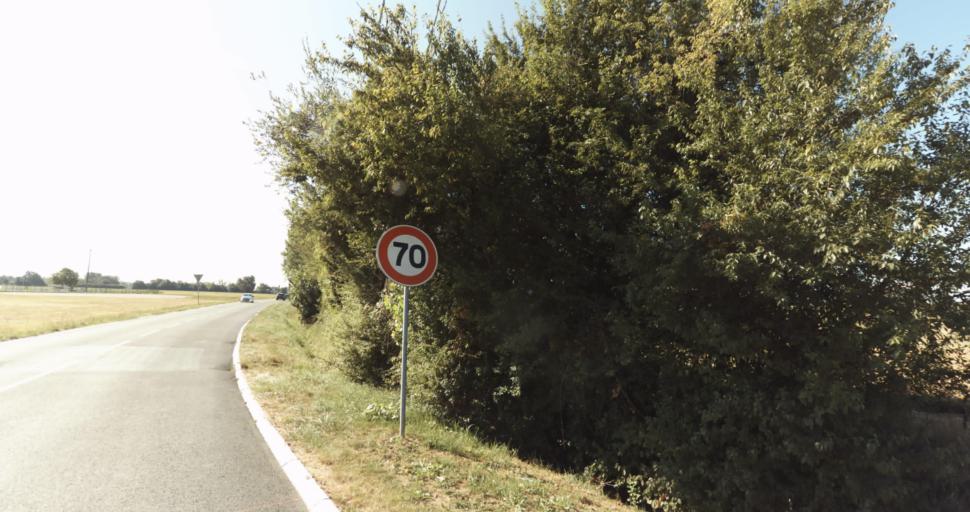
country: FR
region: Midi-Pyrenees
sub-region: Departement de la Haute-Garonne
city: Launaguet
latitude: 43.6702
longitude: 1.4573
